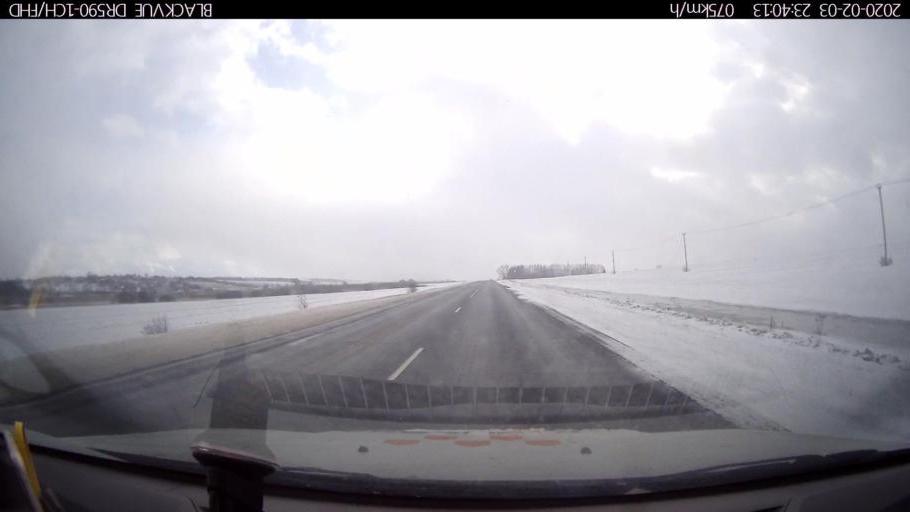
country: RU
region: Nizjnij Novgorod
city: Dal'neye Konstantinovo
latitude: 55.8755
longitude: 44.1357
